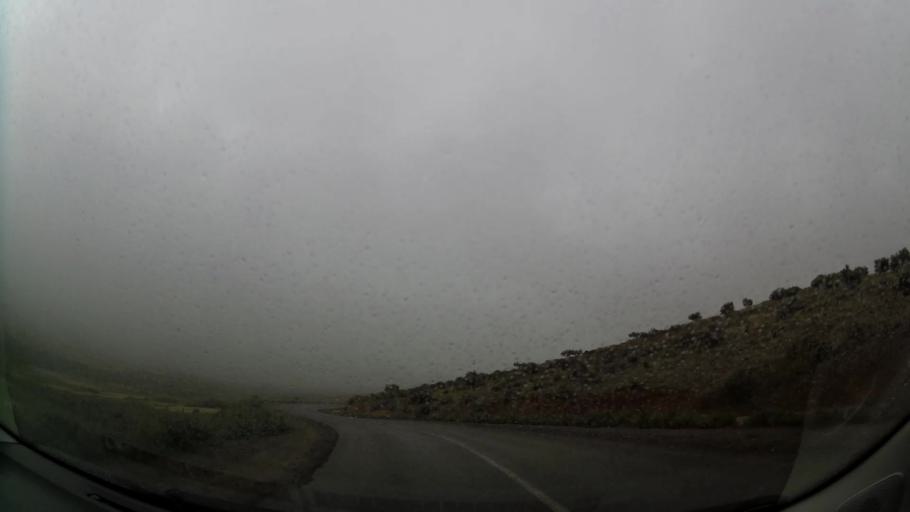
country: MA
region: Oriental
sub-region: Nador
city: Boudinar
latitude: 35.1348
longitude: -3.5977
